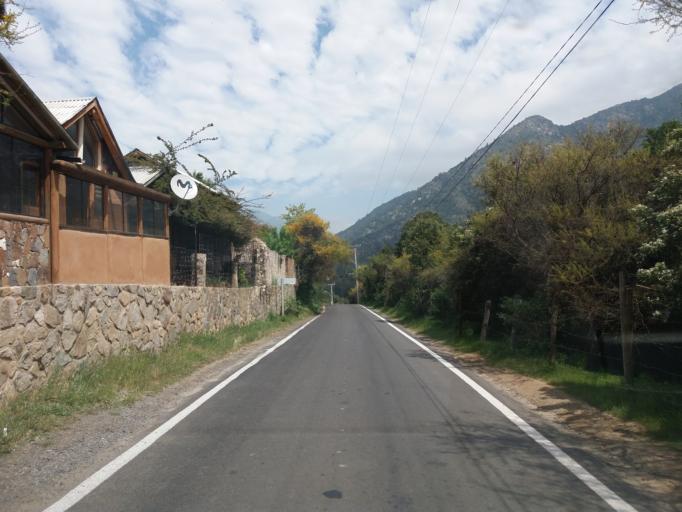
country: CL
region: Valparaiso
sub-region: Provincia de Marga Marga
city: Limache
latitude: -33.0263
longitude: -71.0764
